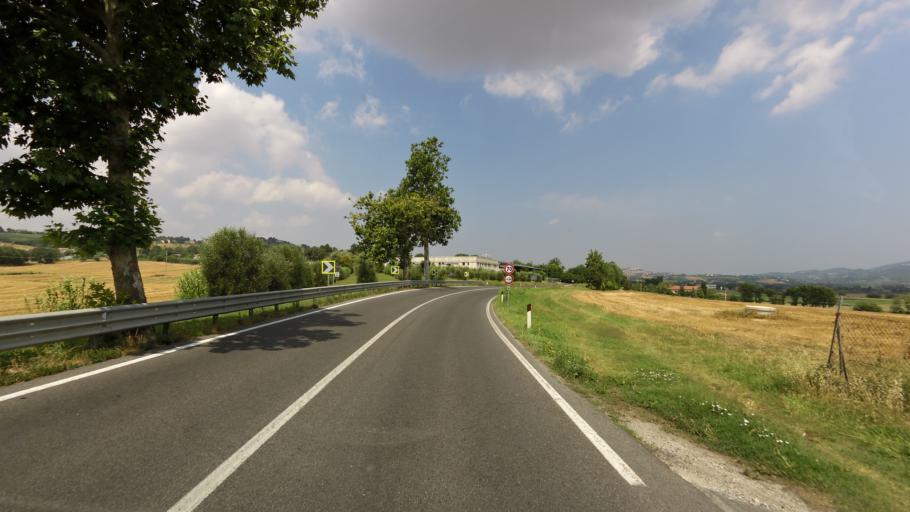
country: IT
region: The Marches
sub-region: Provincia di Ancona
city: Castelfidardo
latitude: 43.4769
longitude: 13.5812
